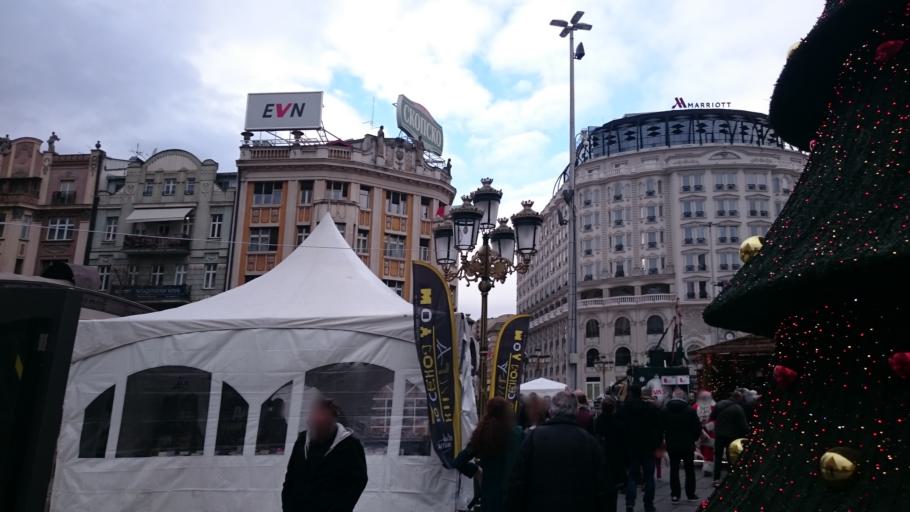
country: MK
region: Karpos
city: Skopje
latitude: 41.9955
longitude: 21.4318
